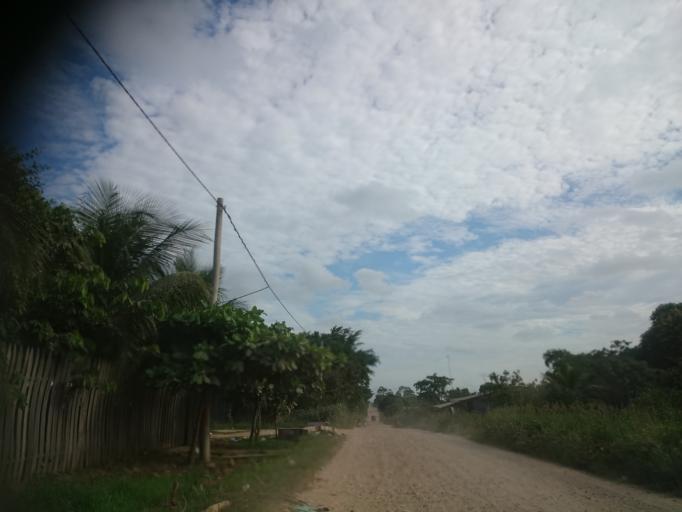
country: PE
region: Ucayali
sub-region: Provincia de Coronel Portillo
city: Puerto Callao
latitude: -8.3754
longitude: -74.5991
